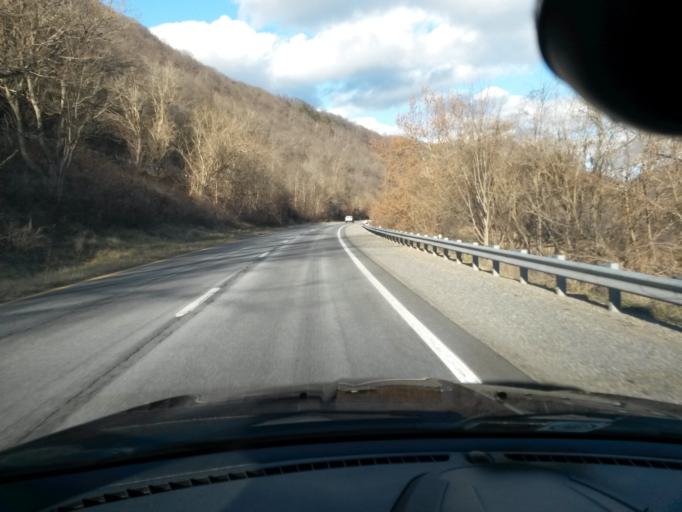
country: US
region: Virginia
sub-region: Giles County
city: Narrows
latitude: 37.3806
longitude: -80.8466
